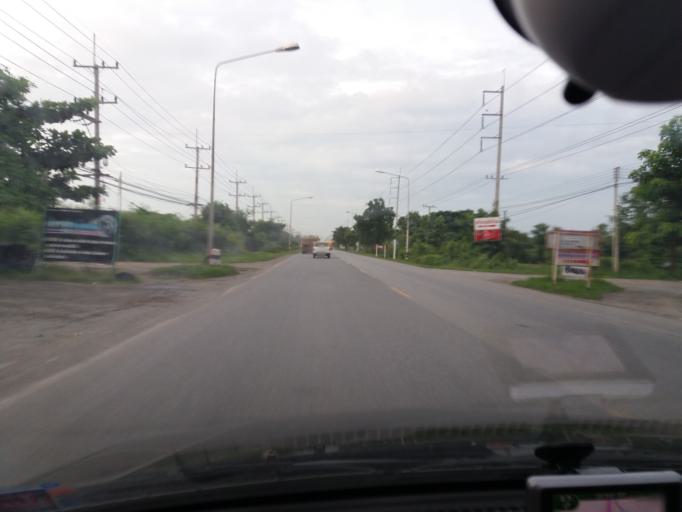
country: TH
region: Suphan Buri
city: U Thong
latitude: 14.4020
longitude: 99.8964
